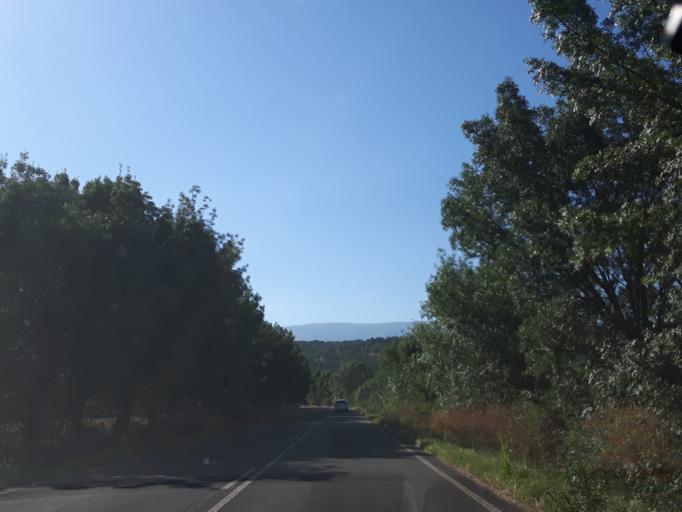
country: ES
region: Castille and Leon
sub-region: Provincia de Salamanca
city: Navalmoral de Bejar
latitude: 40.4205
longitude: -5.8103
